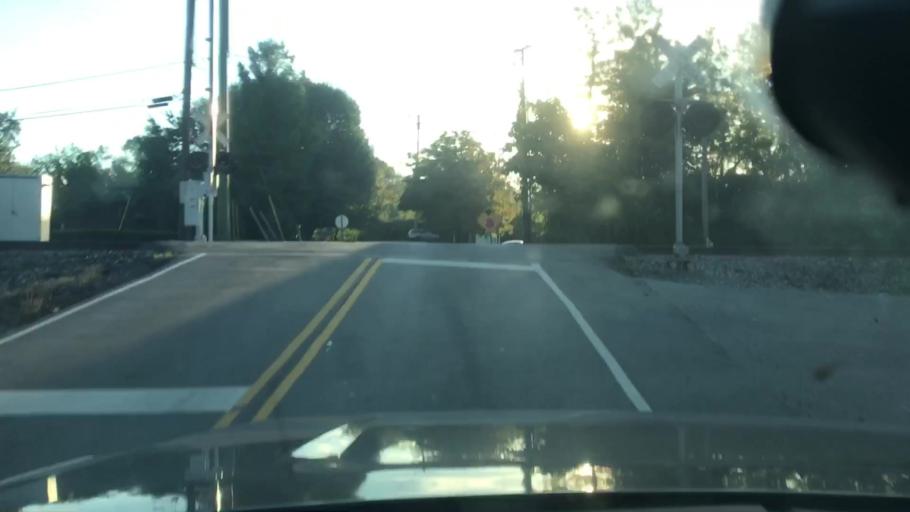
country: US
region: Tennessee
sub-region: Williamson County
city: Brentwood Estates
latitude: 36.0213
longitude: -86.7890
